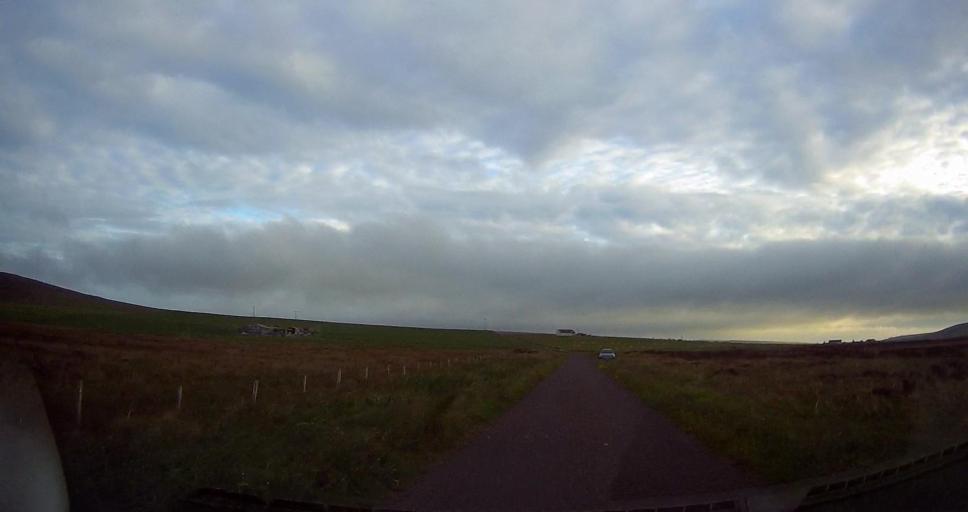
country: GB
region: Scotland
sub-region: Orkney Islands
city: Stromness
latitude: 59.1089
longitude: -3.2320
